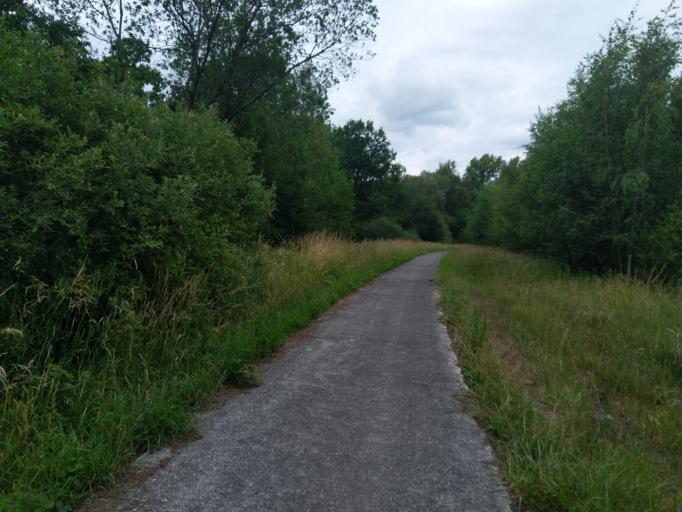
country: BE
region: Wallonia
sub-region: Province du Hainaut
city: Bernissart
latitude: 50.4825
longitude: 3.6379
